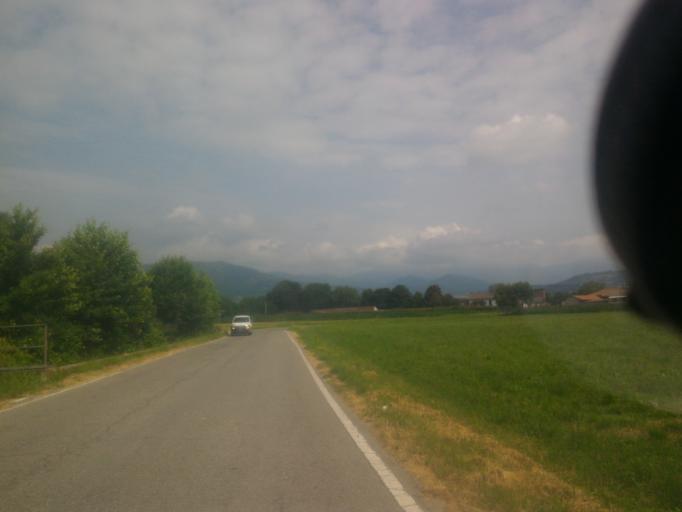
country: IT
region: Piedmont
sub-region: Provincia di Torino
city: San Secondo di Pinerolo
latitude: 44.8596
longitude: 7.3203
